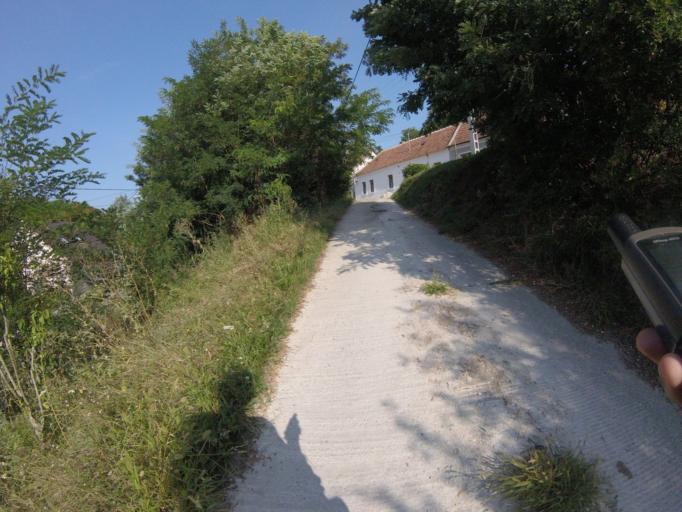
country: HU
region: Gyor-Moson-Sopron
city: Fertorakos
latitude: 47.7226
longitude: 16.6418
